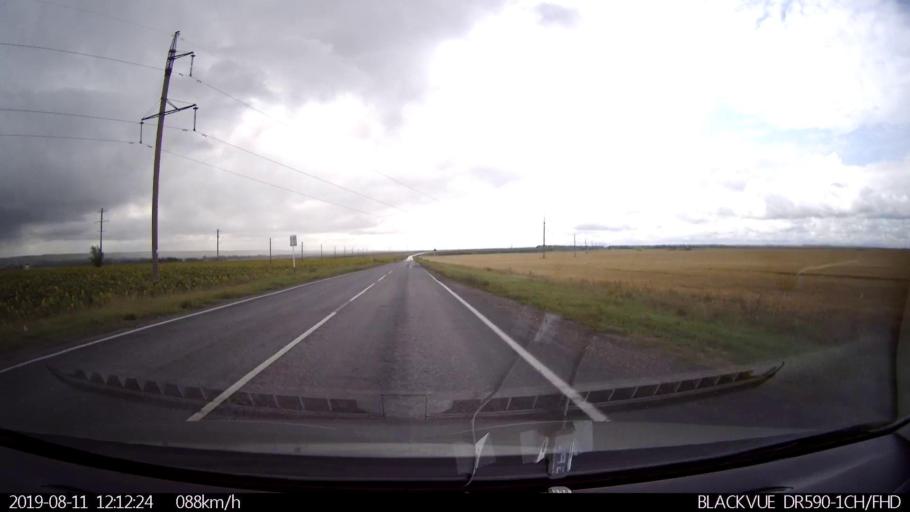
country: RU
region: Ulyanovsk
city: Silikatnyy
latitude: 53.9736
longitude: 47.9968
